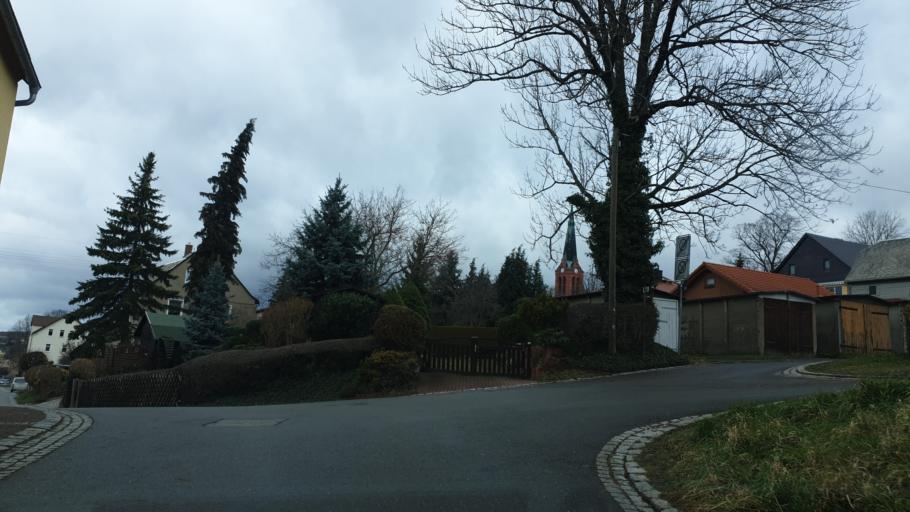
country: DE
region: Saxony
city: Hohndorf
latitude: 50.7437
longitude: 12.6745
